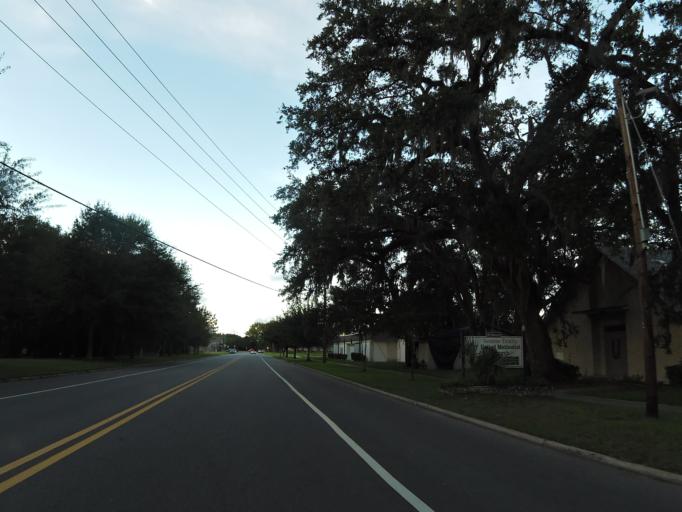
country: US
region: Georgia
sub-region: Camden County
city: St. Marys
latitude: 30.7321
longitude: -81.5459
